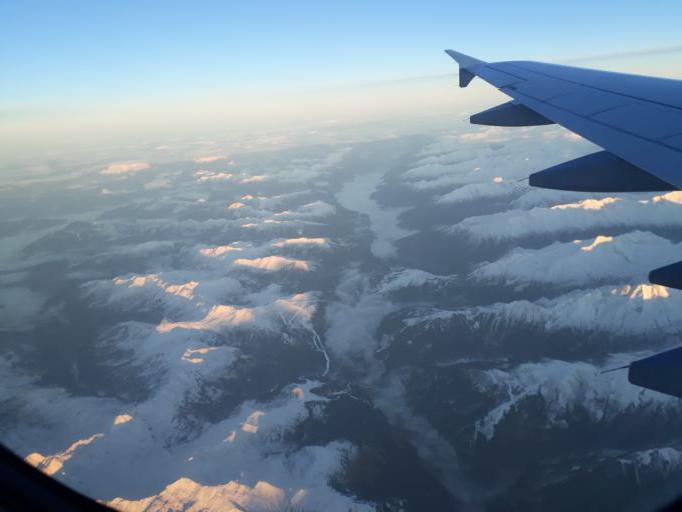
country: AT
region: Tyrol
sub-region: Politischer Bezirk Schwaz
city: Hainzenberg
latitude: 47.2121
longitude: 11.8959
